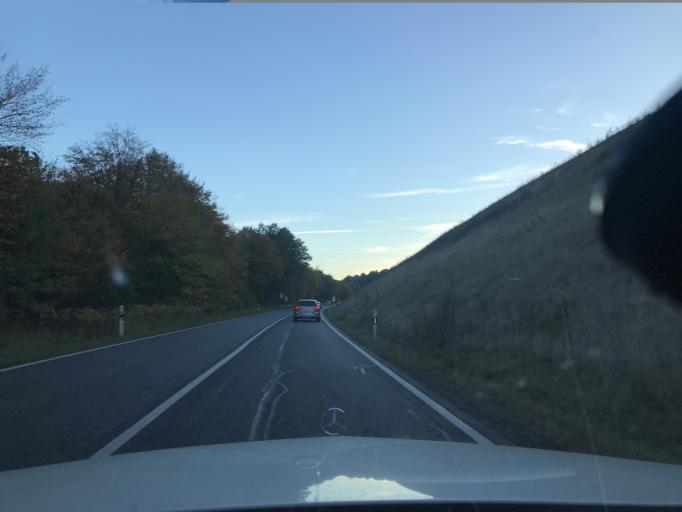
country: DE
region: Hesse
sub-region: Regierungsbezirk Kassel
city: Helsa
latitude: 51.2424
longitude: 9.6803
